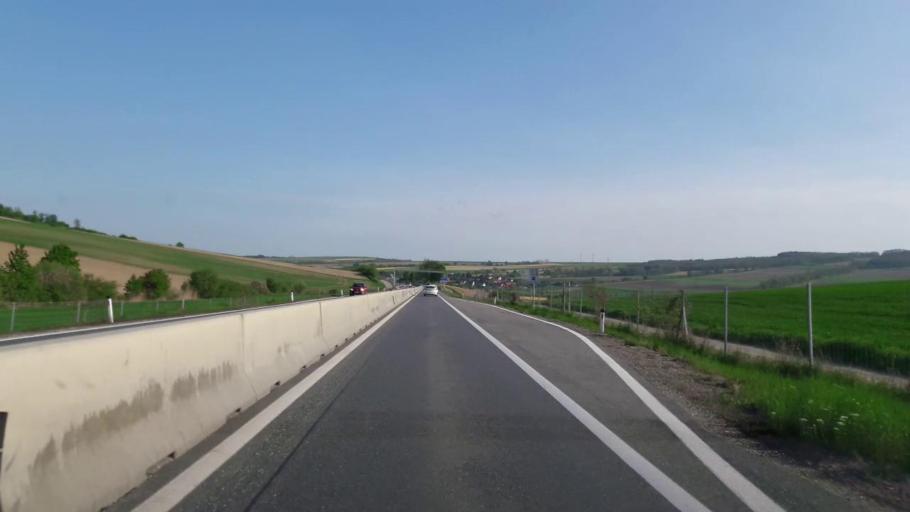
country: AT
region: Lower Austria
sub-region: Politischer Bezirk Hollabrunn
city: Hollabrunn
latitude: 48.5172
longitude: 16.0865
